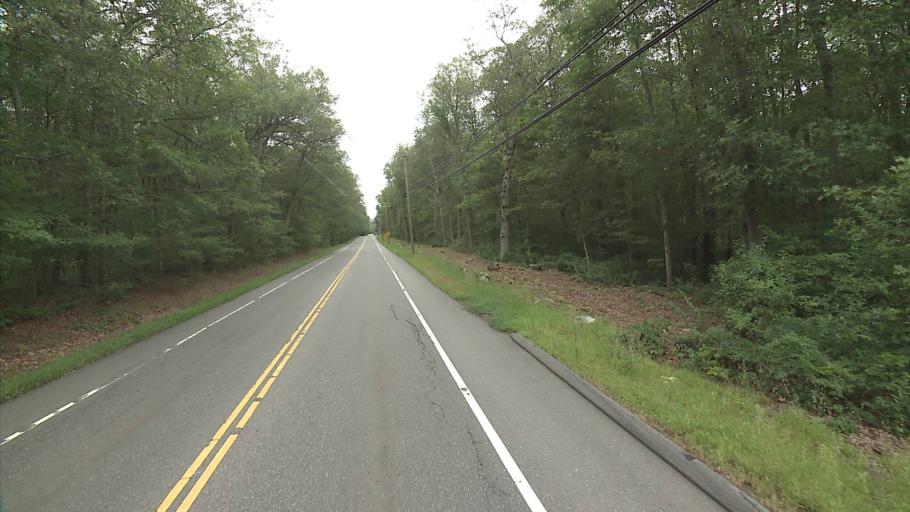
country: US
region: Connecticut
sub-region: New London County
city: Colchester
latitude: 41.6034
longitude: -72.3437
